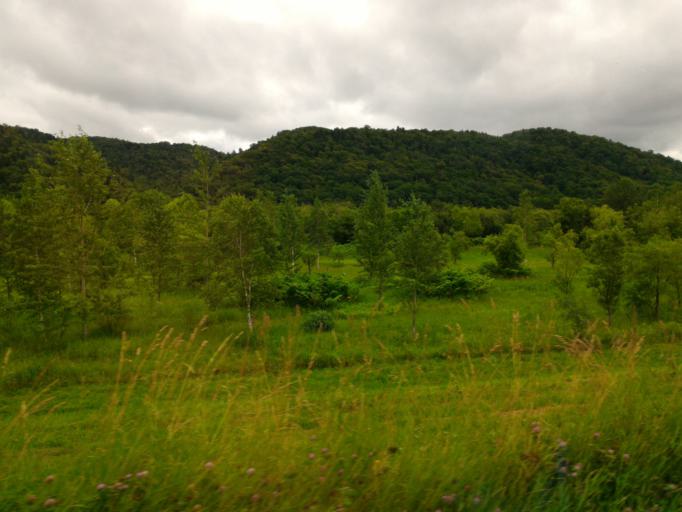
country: JP
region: Hokkaido
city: Nayoro
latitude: 44.7937
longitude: 142.0667
